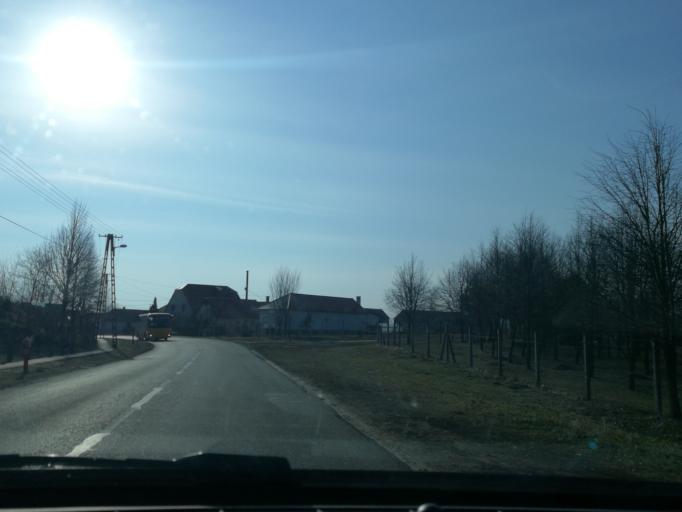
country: HU
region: Szabolcs-Szatmar-Bereg
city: Levelek
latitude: 48.0457
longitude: 21.9737
